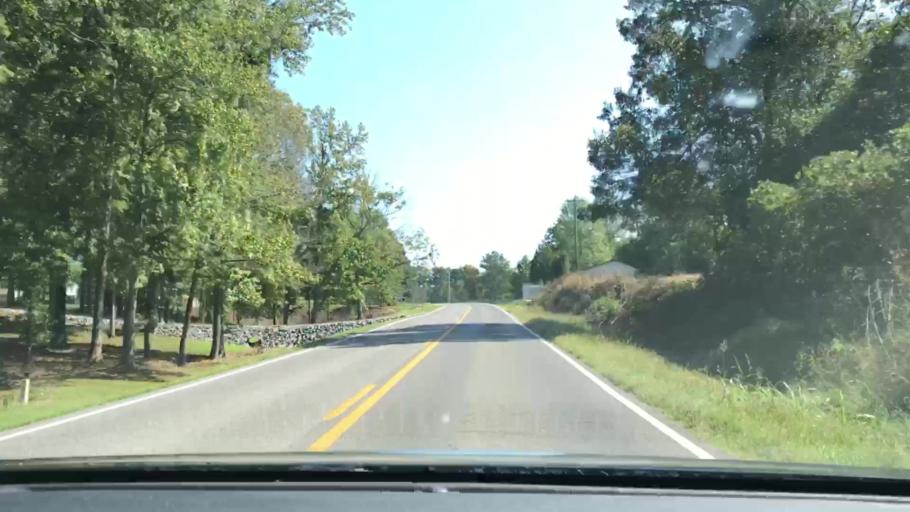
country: US
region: Kentucky
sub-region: Marshall County
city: Benton
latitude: 36.7668
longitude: -88.1842
